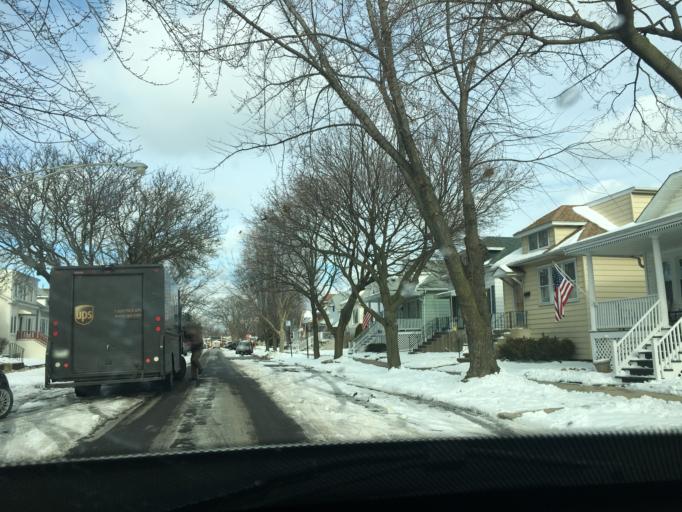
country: US
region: Illinois
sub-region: Cook County
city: Harwood Heights
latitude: 41.9478
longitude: -87.8132
